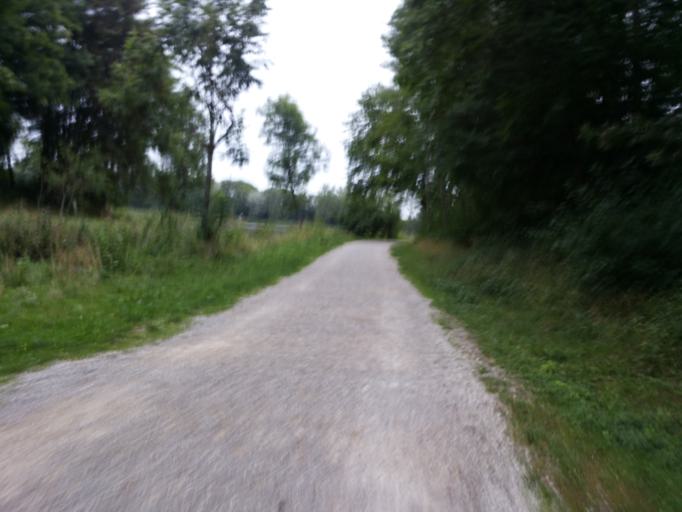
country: DE
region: Bavaria
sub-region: Upper Bavaria
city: Ingolstadt
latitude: 48.7452
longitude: 11.3856
